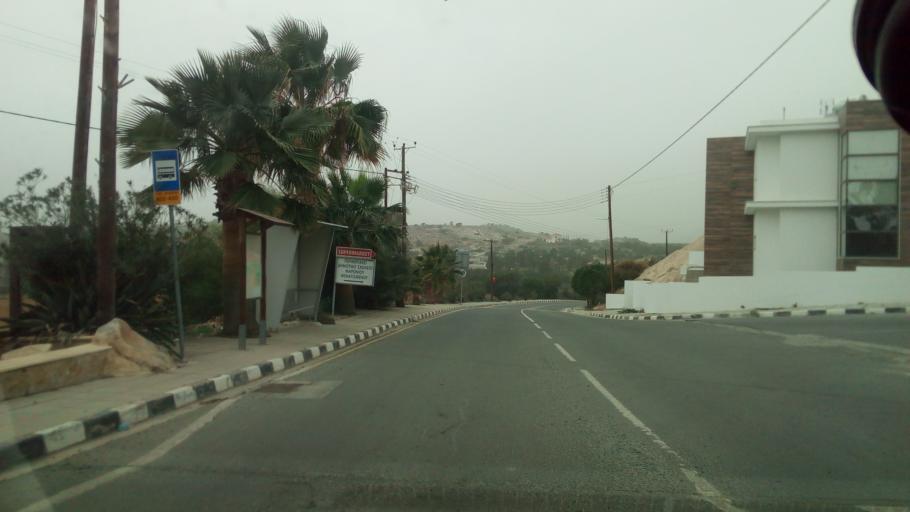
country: CY
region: Larnaka
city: Kofinou
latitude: 34.7580
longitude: 33.3530
